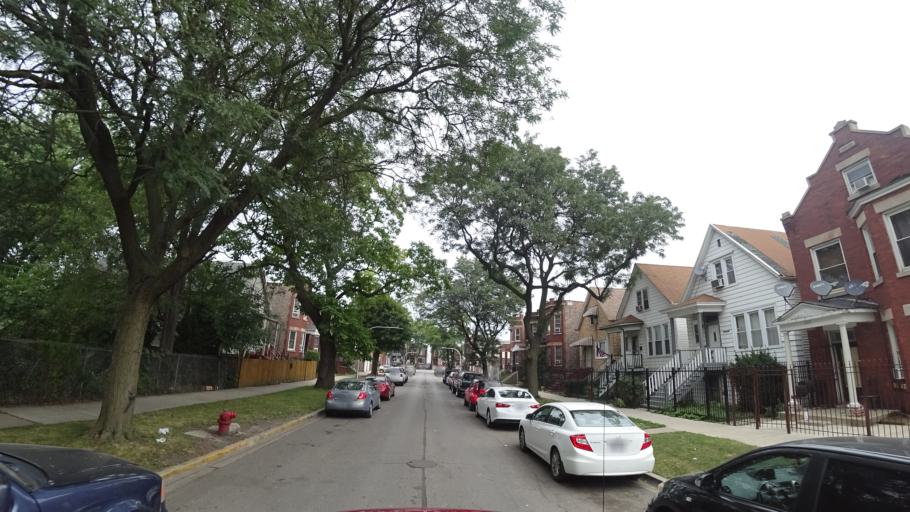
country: US
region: Illinois
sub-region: Cook County
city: Cicero
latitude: 41.8503
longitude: -87.7334
